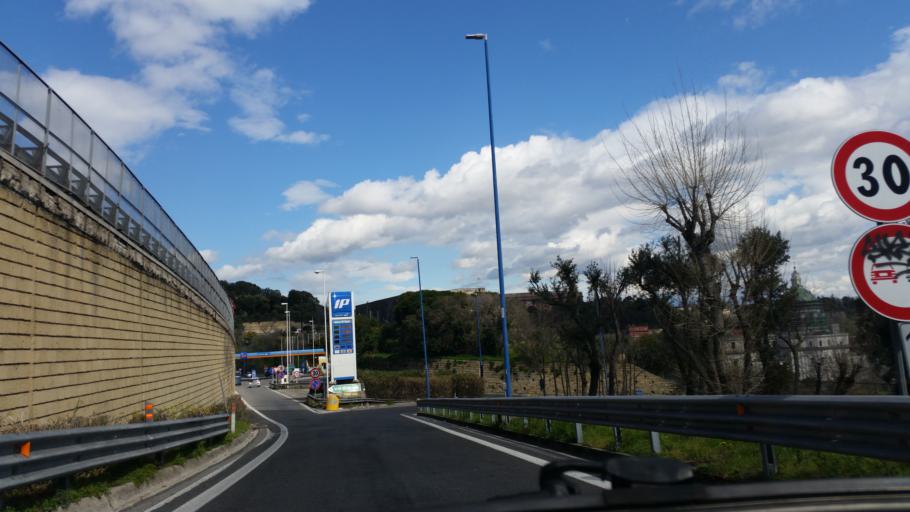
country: IT
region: Campania
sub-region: Provincia di Napoli
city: Napoli
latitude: 40.8648
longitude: 14.2417
